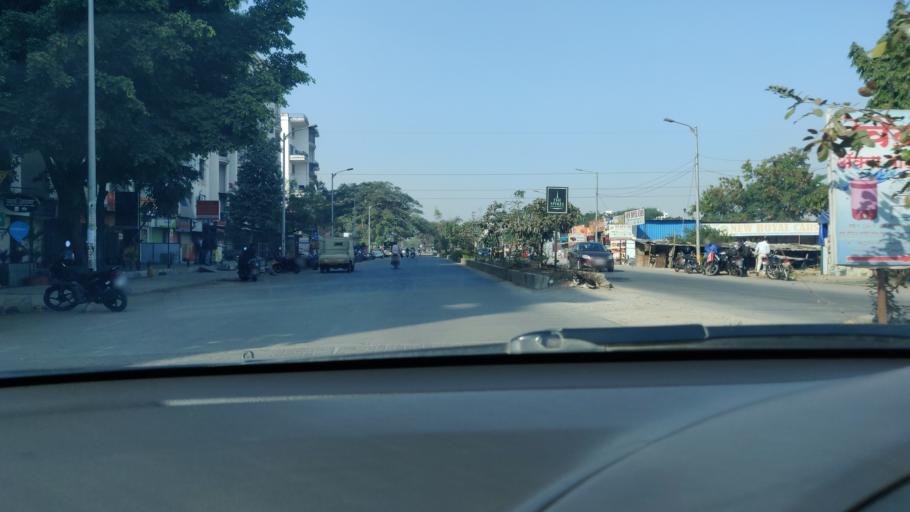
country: IN
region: Maharashtra
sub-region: Pune Division
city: Khadki
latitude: 18.5655
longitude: 73.8016
